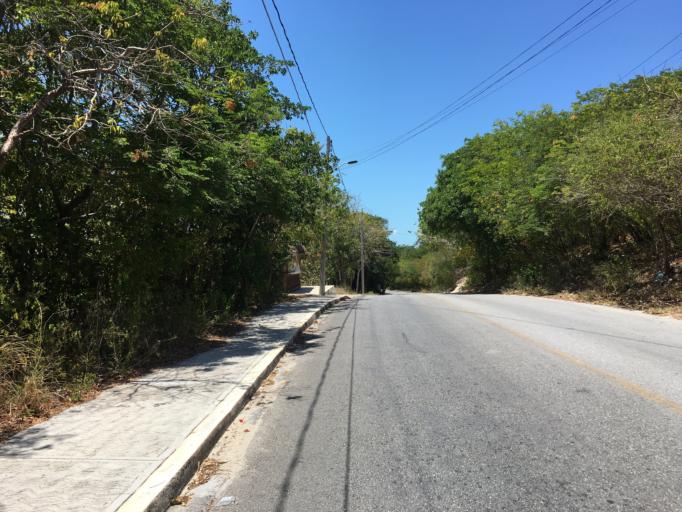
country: MX
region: Quintana Roo
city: Isla Mujeres
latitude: 21.2146
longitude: -86.7239
